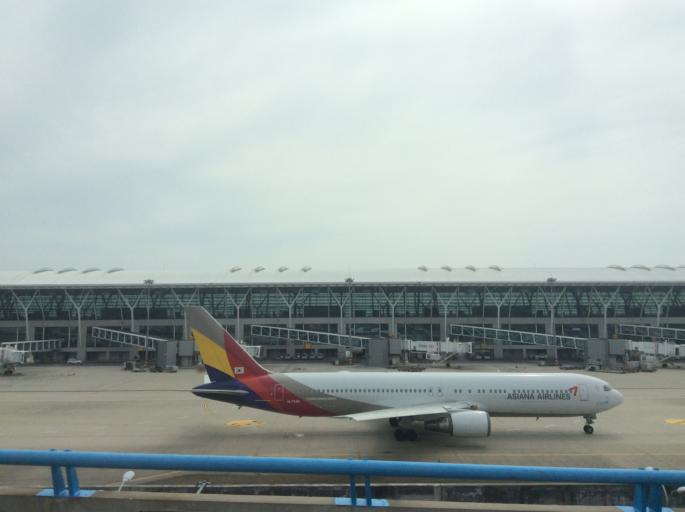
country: CN
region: Shanghai Shi
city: Laogang
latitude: 31.1496
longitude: 121.8052
